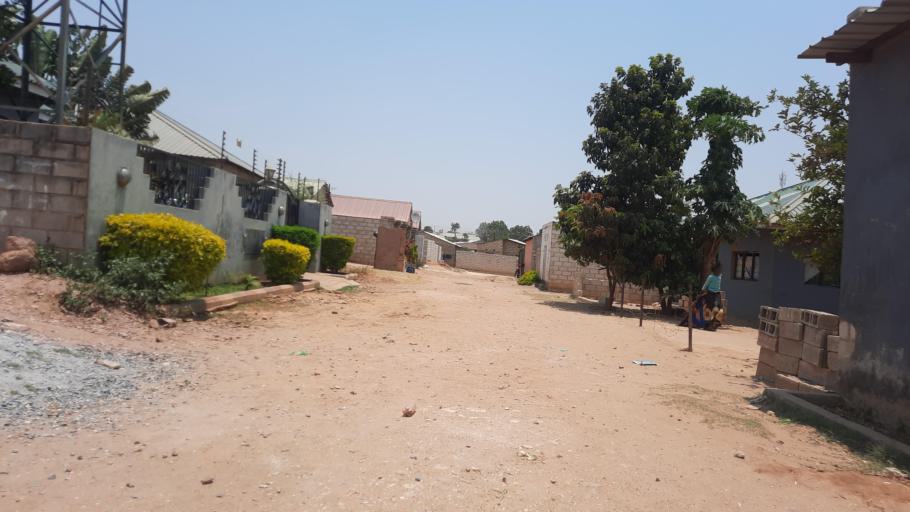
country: ZM
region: Lusaka
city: Lusaka
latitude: -15.4044
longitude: 28.3824
